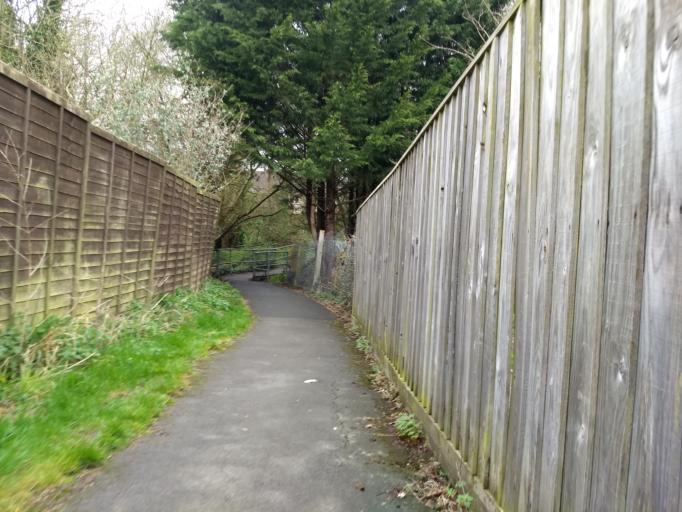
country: GB
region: England
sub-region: Isle of Wight
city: Ryde
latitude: 50.7237
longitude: -1.1829
